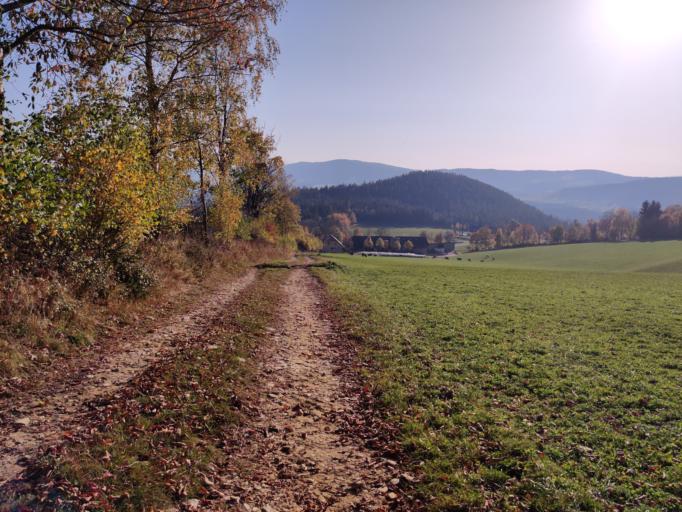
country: AT
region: Styria
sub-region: Politischer Bezirk Hartberg-Fuerstenfeld
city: Sankt Jakob im Walde
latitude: 47.4688
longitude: 15.8106
